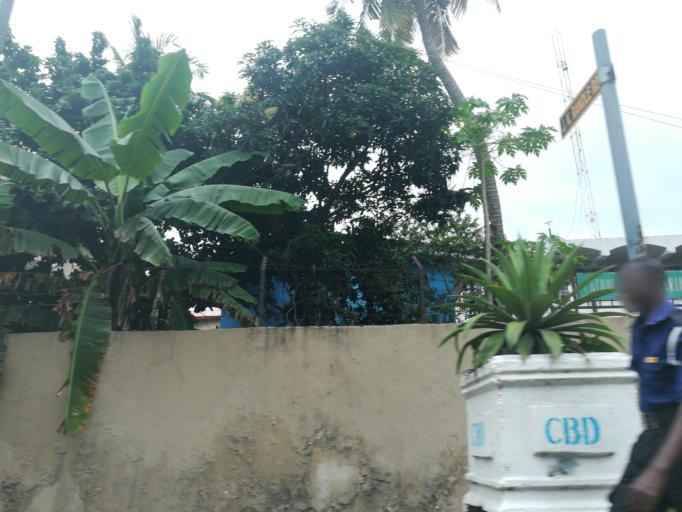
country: NG
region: Lagos
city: Lagos
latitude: 6.4445
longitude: 3.4013
